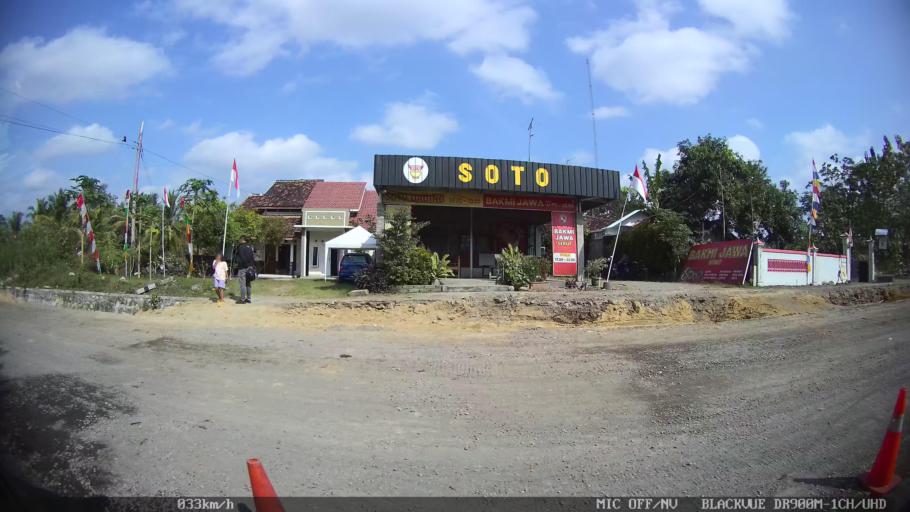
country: ID
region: Daerah Istimewa Yogyakarta
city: Godean
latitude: -7.8281
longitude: 110.2218
